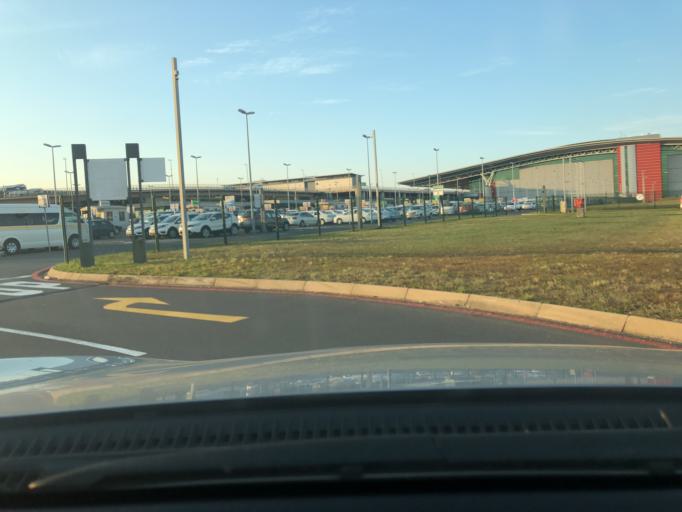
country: ZA
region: KwaZulu-Natal
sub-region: iLembe District Municipality
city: Ballitoville
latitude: -29.6218
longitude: 31.1030
